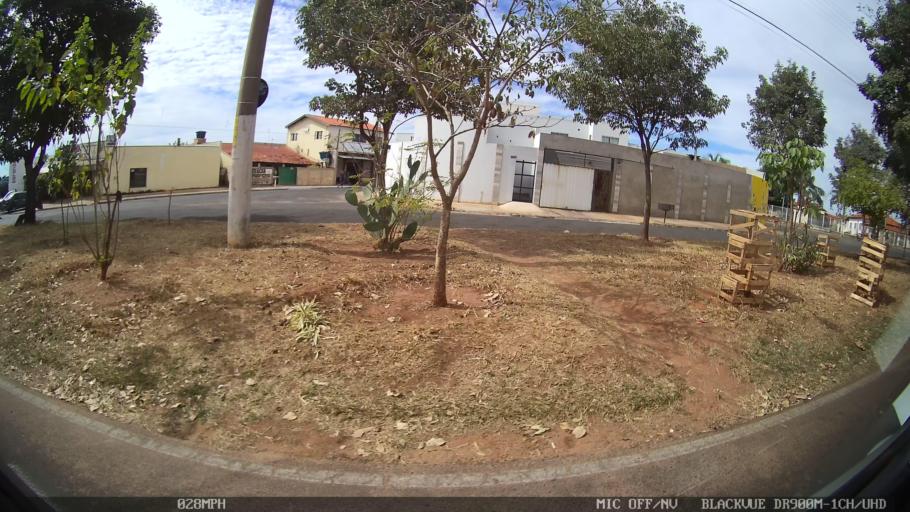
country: BR
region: Sao Paulo
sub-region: Catanduva
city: Catanduva
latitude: -21.1665
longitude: -48.9697
